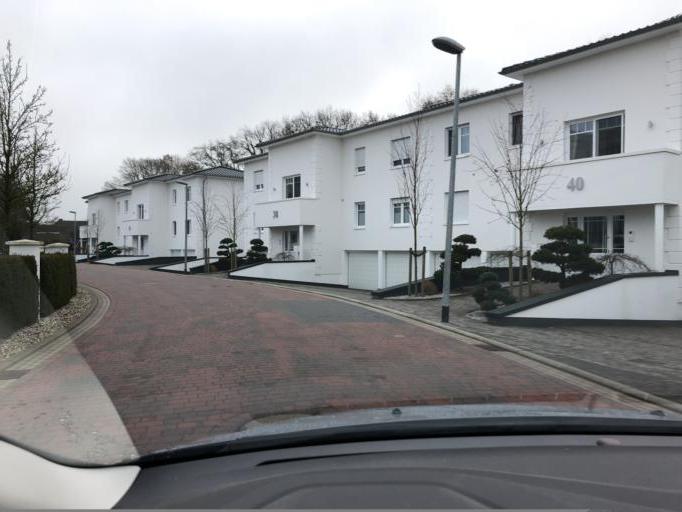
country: DE
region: Lower Saxony
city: Bad Zwischenahn
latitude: 53.1773
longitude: 8.0155
